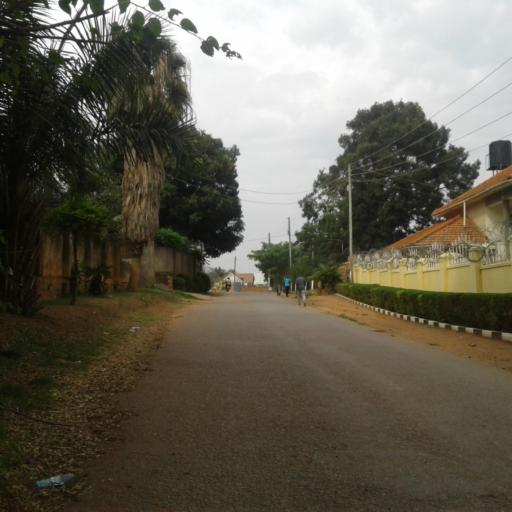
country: UG
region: Central Region
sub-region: Kampala District
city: Kampala
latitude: 0.2779
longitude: 32.6195
